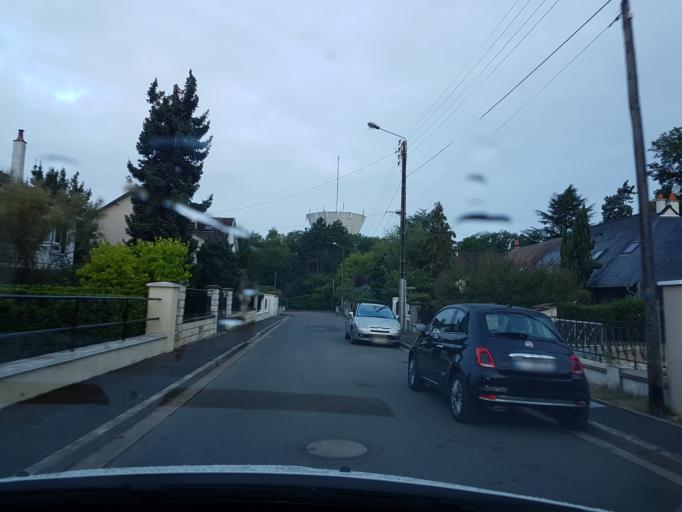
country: FR
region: Centre
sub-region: Departement d'Indre-et-Loire
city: Saint-Avertin
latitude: 47.3680
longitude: 0.7469
